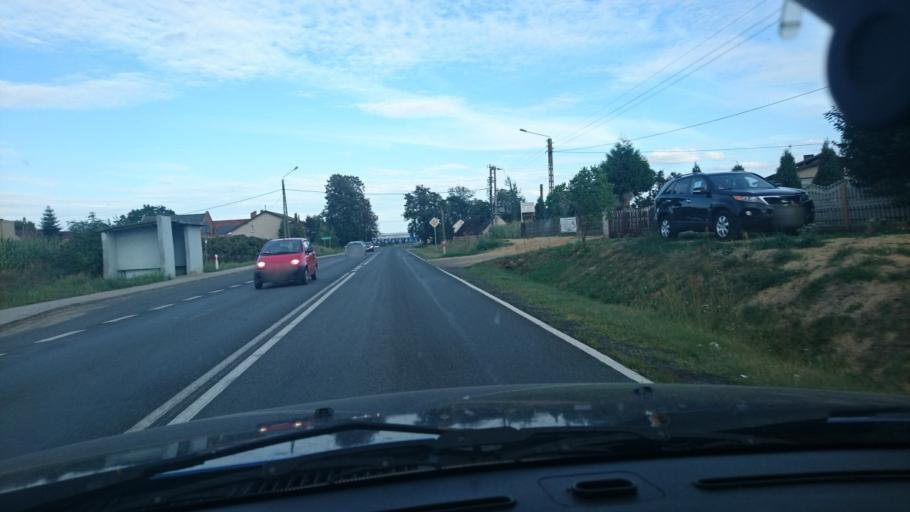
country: PL
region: Greater Poland Voivodeship
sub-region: Powiat kepinski
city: Slupia pod Kepnem
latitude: 51.2307
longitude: 18.0743
